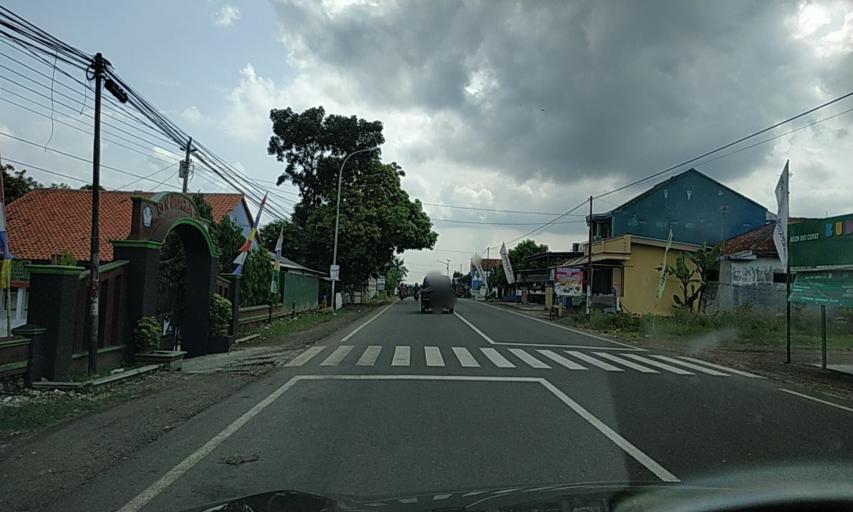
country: ID
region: Central Java
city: Wanareja
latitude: -7.3353
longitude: 108.6856
